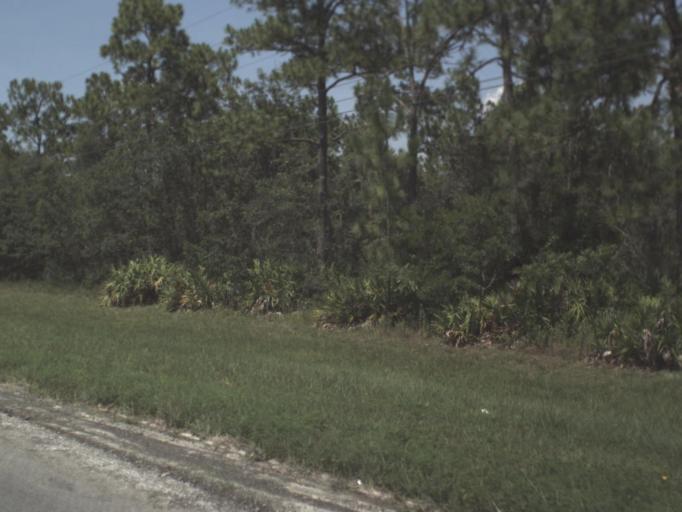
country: US
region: Florida
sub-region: Citrus County
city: Sugarmill Woods
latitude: 28.6898
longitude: -82.5523
